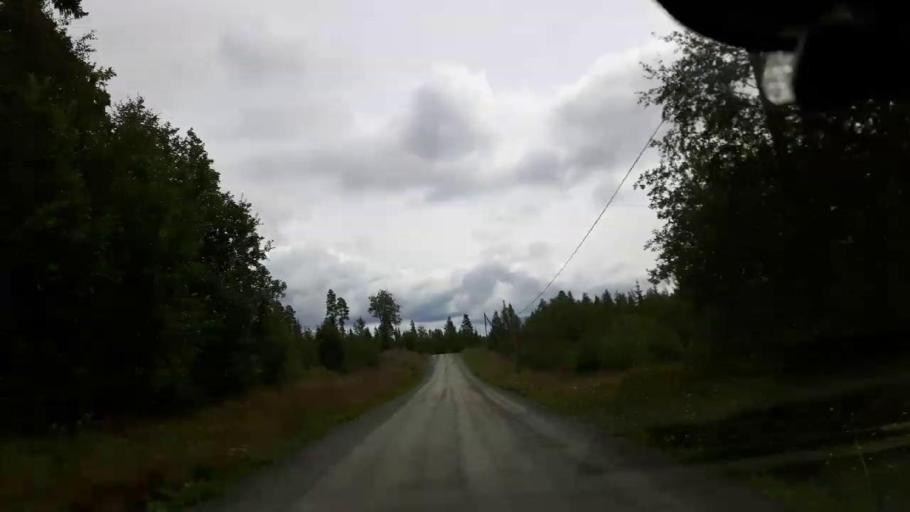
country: SE
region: Jaemtland
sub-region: Krokoms Kommun
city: Valla
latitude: 63.6857
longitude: 13.9136
